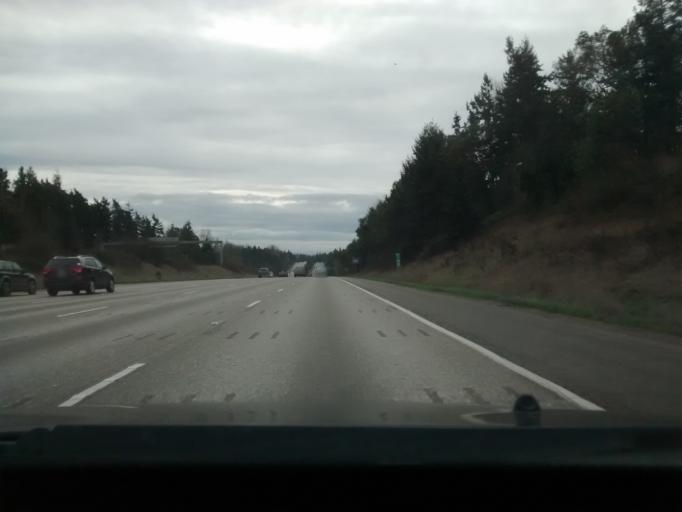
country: US
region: Washington
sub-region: King County
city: Des Moines
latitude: 47.3742
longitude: -122.2927
